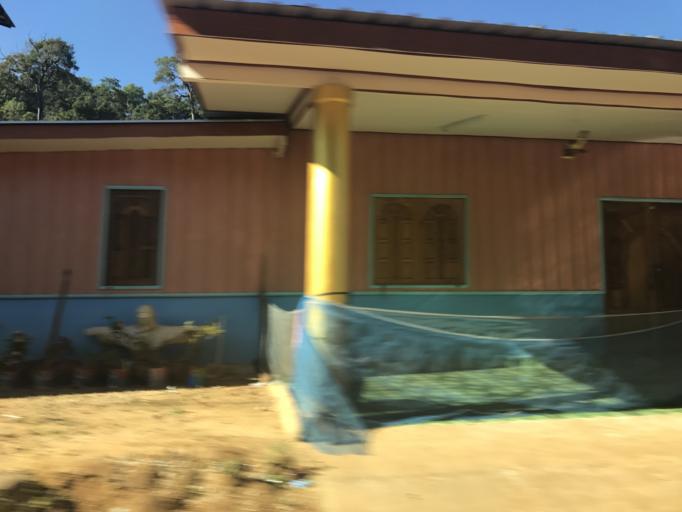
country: TH
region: Tak
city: Phop Phra
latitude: 16.5666
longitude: 98.8142
